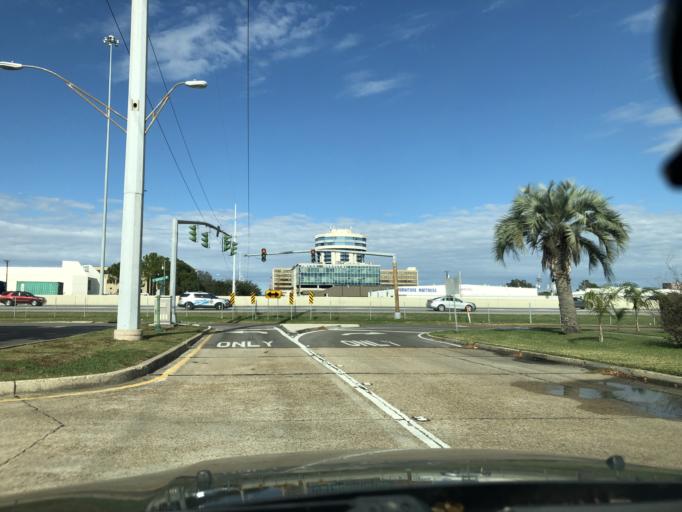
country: US
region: Louisiana
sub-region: Jefferson Parish
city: Metairie
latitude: 29.9968
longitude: -90.1597
